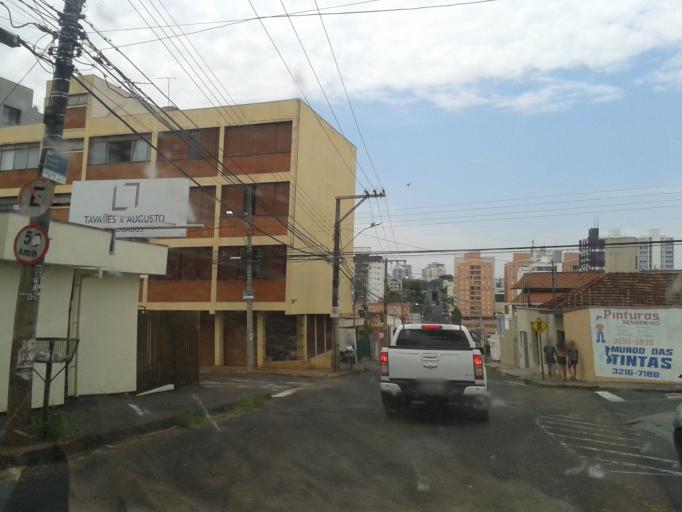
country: BR
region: Minas Gerais
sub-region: Uberlandia
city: Uberlandia
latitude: -18.9178
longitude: -48.2686
